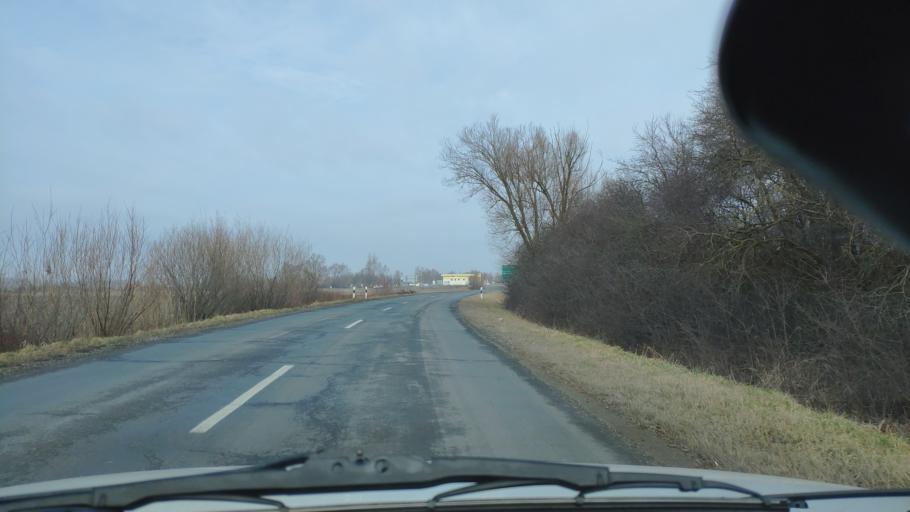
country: HU
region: Zala
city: Nagykanizsa
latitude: 46.4630
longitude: 16.9686
